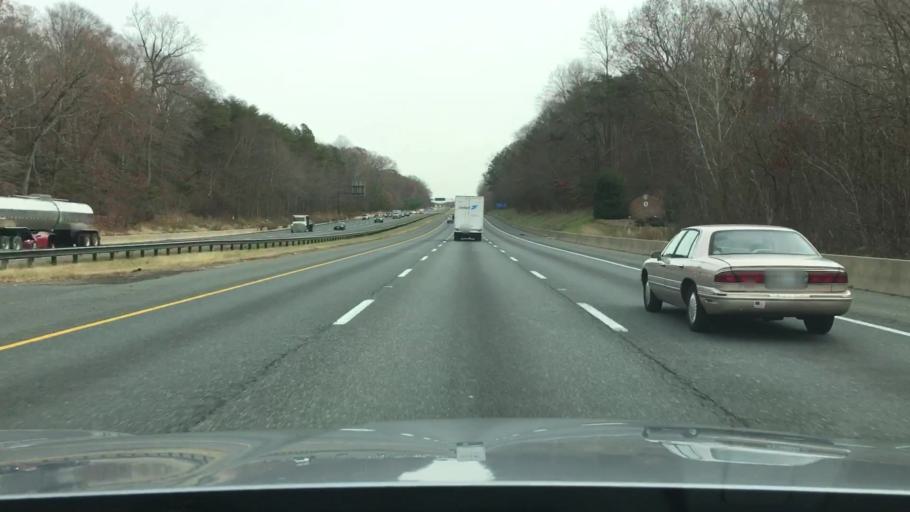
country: US
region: Maryland
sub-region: Prince George's County
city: Bowie
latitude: 38.9556
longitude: -76.6922
